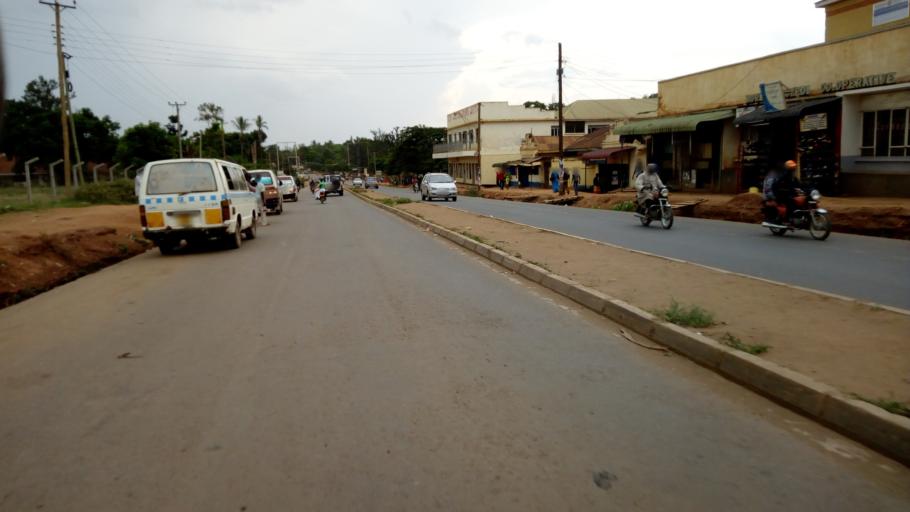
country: UG
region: Eastern Region
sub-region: Mbale District
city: Mbale
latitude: 1.0766
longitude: 34.1751
